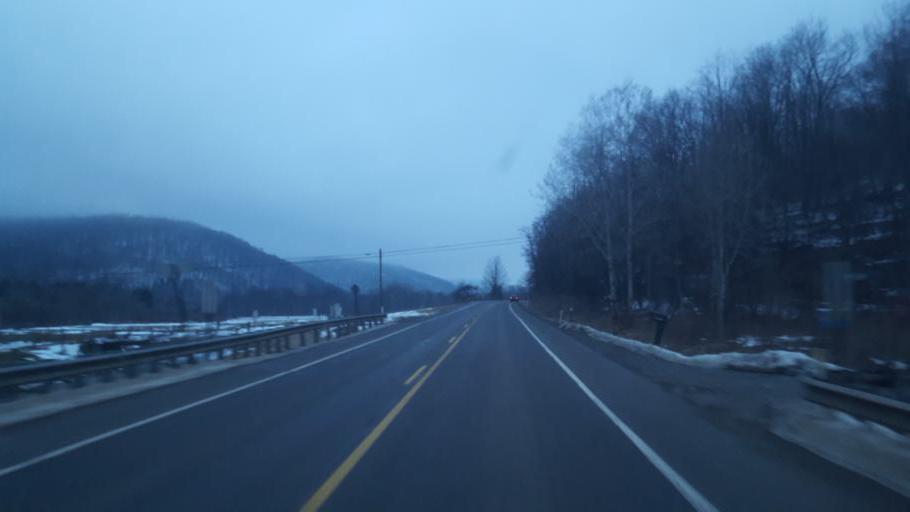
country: US
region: Pennsylvania
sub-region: Potter County
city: Coudersport
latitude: 41.7442
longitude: -78.0870
